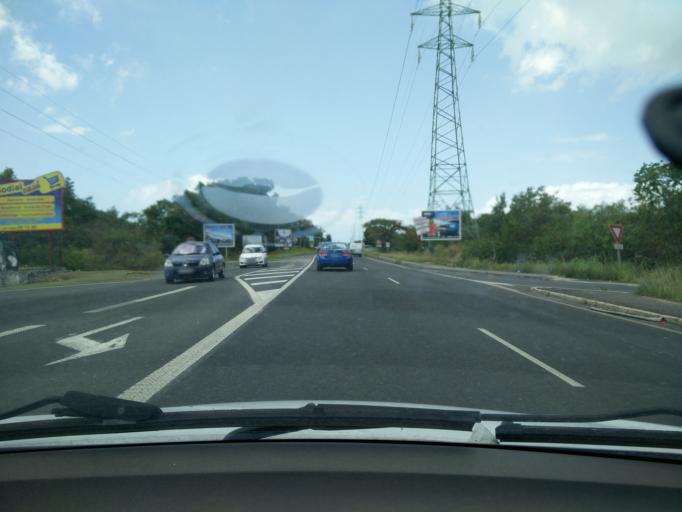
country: GP
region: Guadeloupe
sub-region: Guadeloupe
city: Pointe-a-Pitre
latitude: 16.2516
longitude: -61.5544
